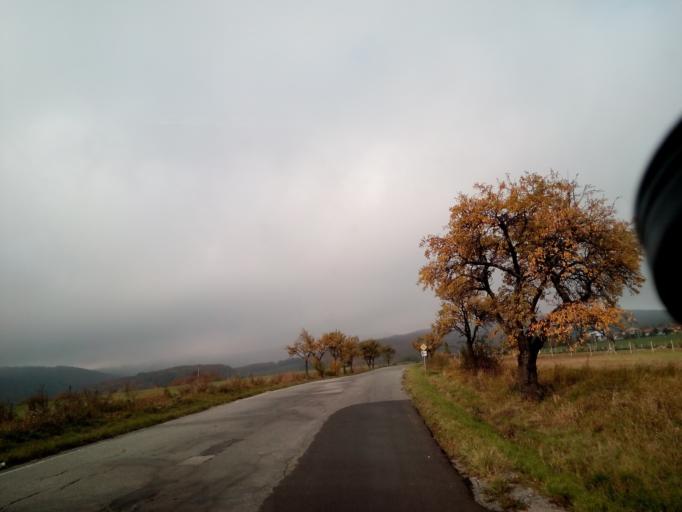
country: SK
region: Kosicky
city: Kosice
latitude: 48.7364
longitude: 21.1254
